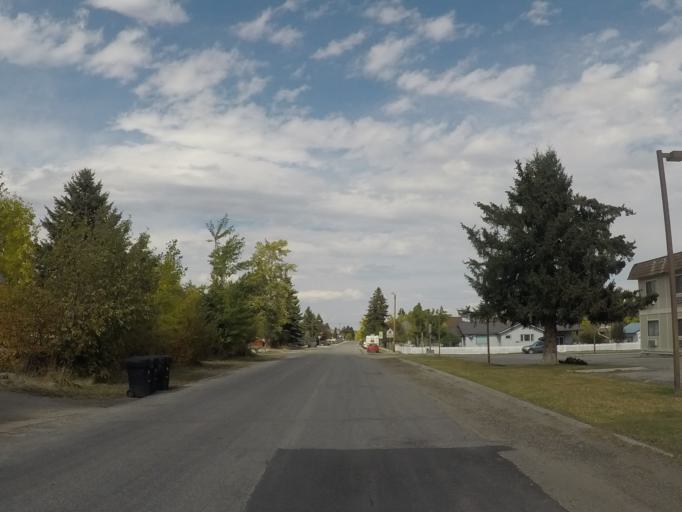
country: US
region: Montana
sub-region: Carbon County
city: Red Lodge
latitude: 45.1794
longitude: -109.2480
